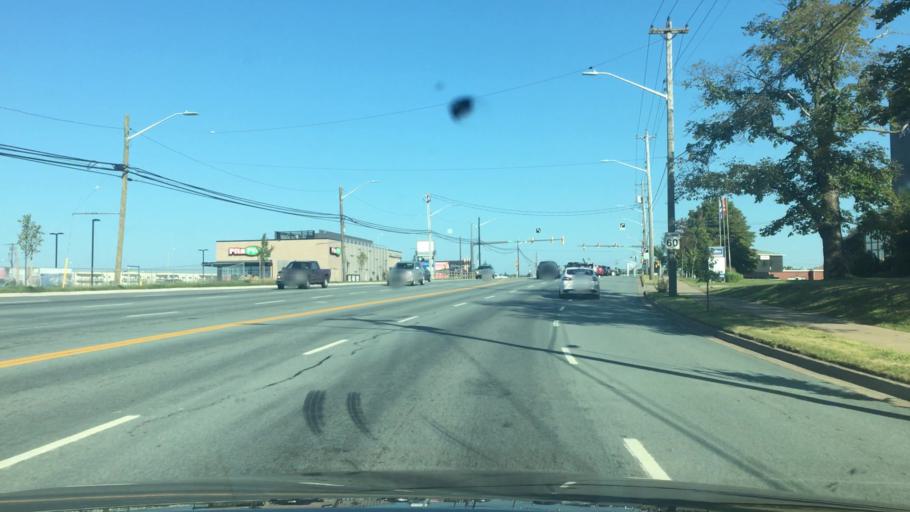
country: CA
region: Nova Scotia
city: Dartmouth
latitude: 44.6993
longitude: -63.6060
